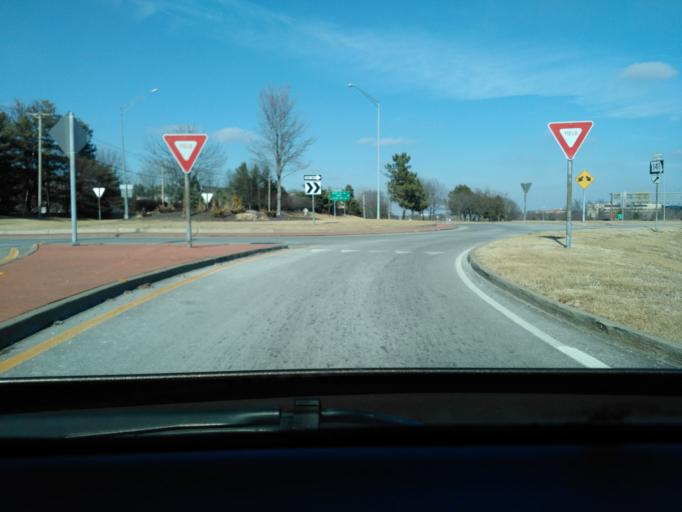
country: US
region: Missouri
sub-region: Saint Louis County
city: Manchester
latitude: 38.6349
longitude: -90.5146
